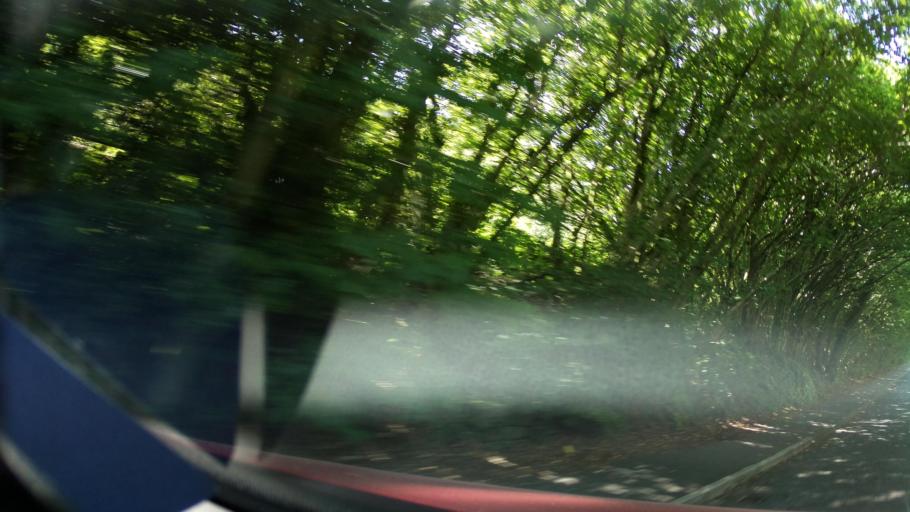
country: GB
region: Wales
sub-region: Caerphilly County Borough
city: Maesycwmmer
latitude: 51.6249
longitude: -3.2309
